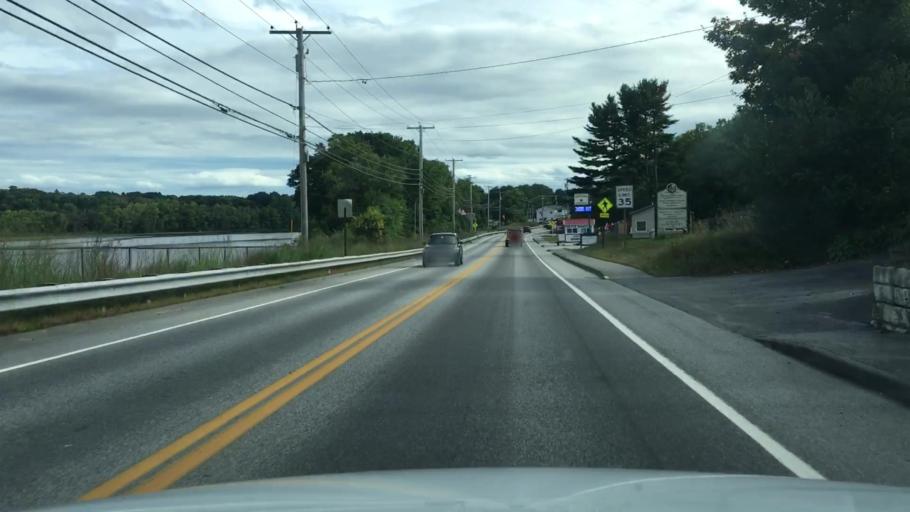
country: US
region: Maine
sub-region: Kennebec County
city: Farmingdale
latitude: 44.2490
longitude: -69.7716
